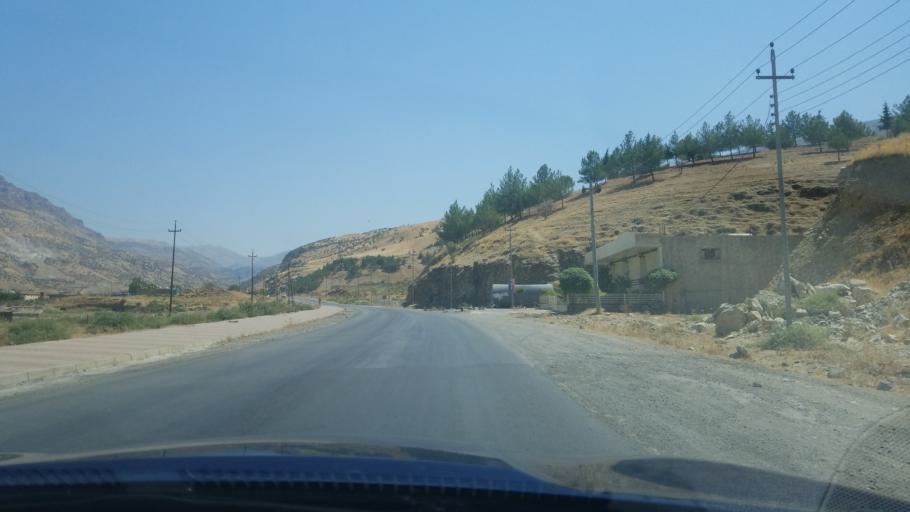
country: IQ
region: Arbil
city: Ruwandiz
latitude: 36.6212
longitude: 44.5402
